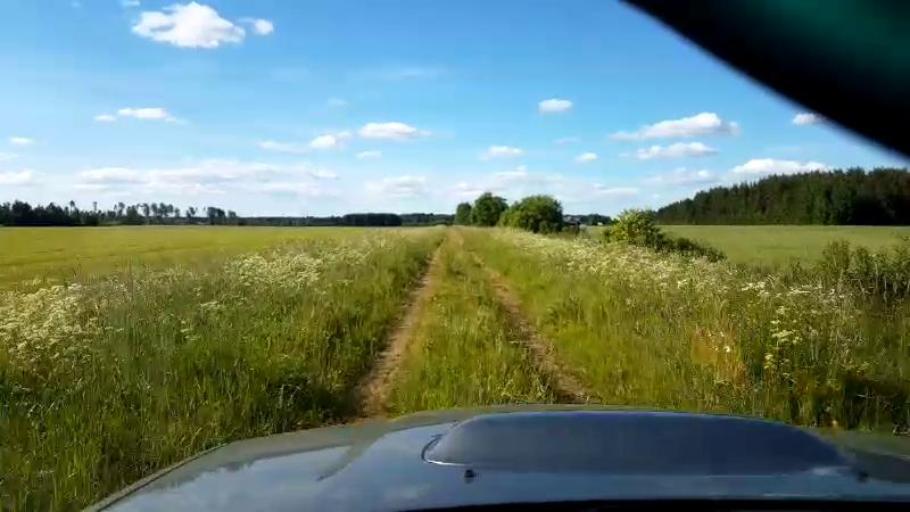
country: EE
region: Paernumaa
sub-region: Sauga vald
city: Sauga
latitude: 58.4998
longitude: 24.5911
